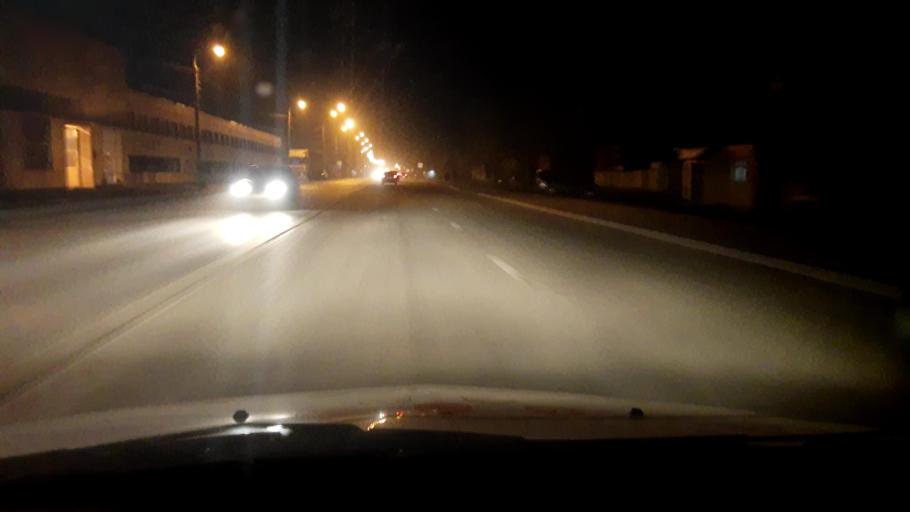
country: RU
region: Bashkortostan
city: Iglino
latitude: 54.7674
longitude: 56.2345
